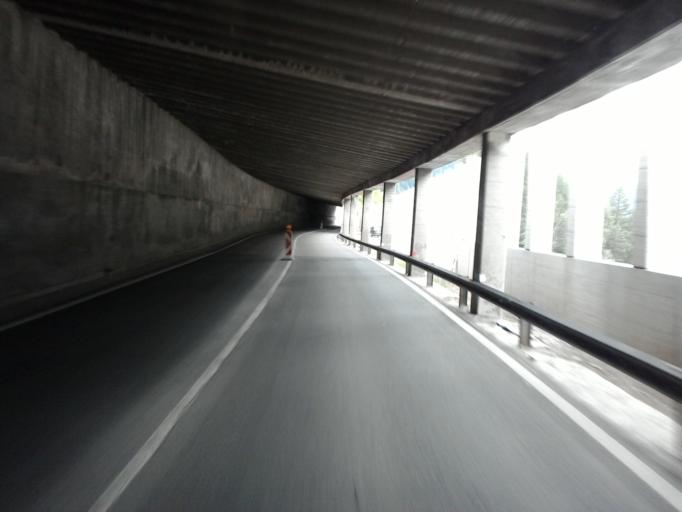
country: AT
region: Tyrol
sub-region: Politischer Bezirk Lienz
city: Matrei in Osttirol
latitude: 47.0766
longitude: 12.5310
